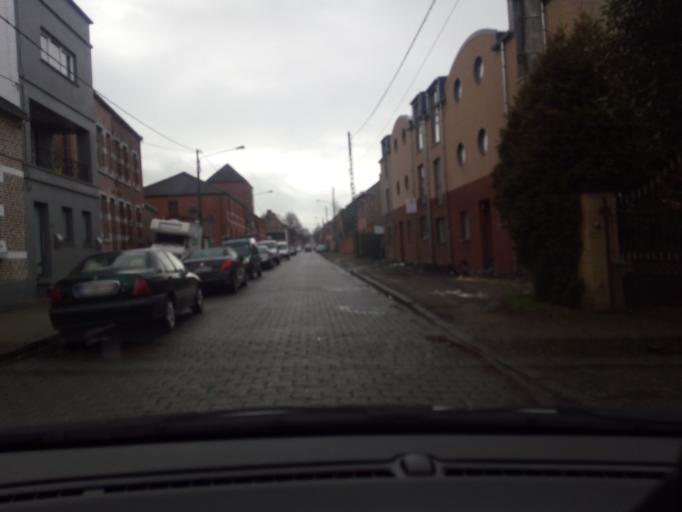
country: BE
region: Wallonia
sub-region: Province du Hainaut
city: Quaregnon
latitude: 50.4256
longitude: 3.8669
